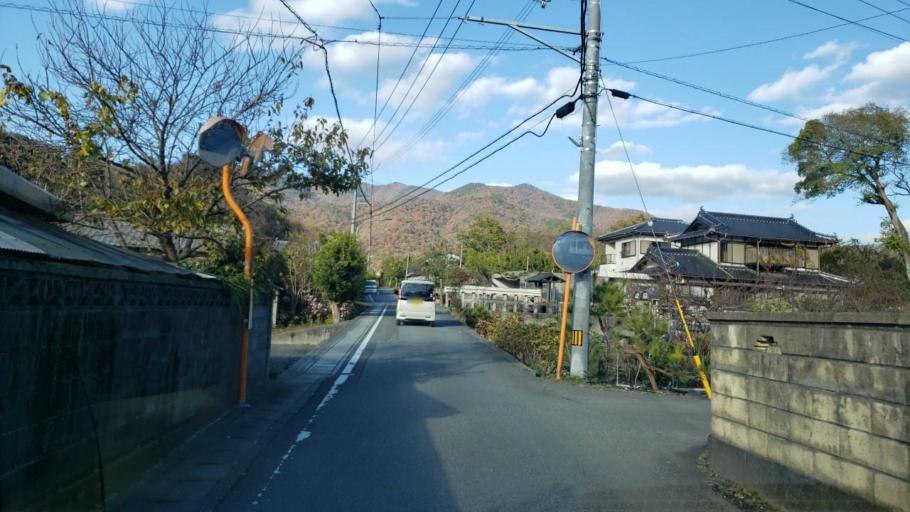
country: JP
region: Tokushima
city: Wakimachi
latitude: 34.0610
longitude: 134.0877
